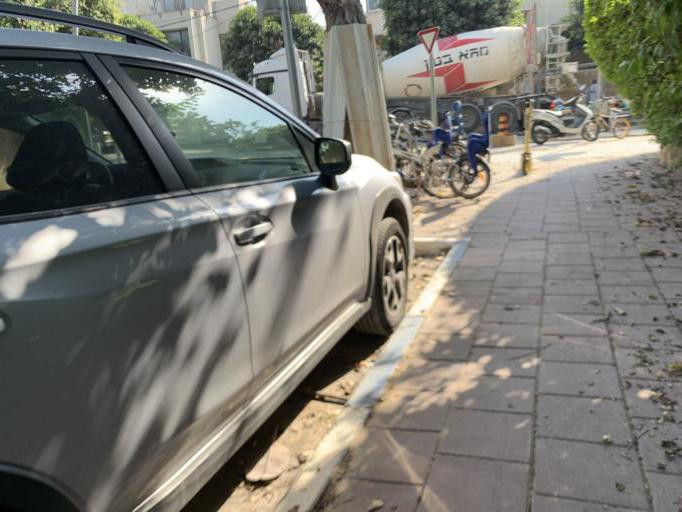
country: IL
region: Tel Aviv
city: Ramat Gan
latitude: 32.0936
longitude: 34.8148
